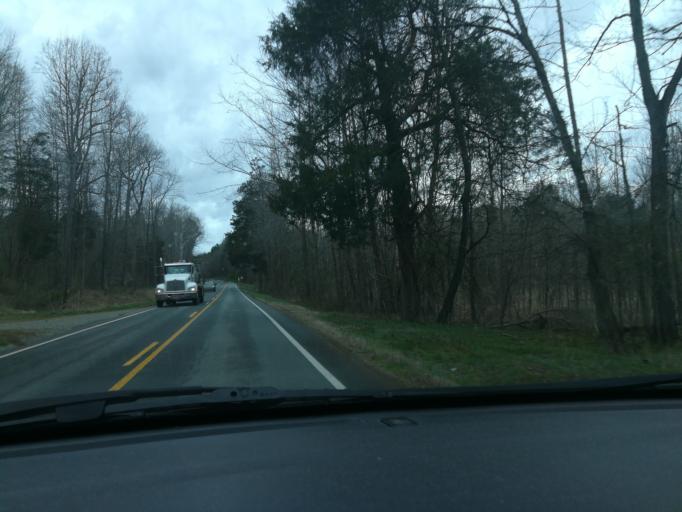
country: US
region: North Carolina
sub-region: Orange County
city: Hillsborough
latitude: 36.0342
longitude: -79.0460
